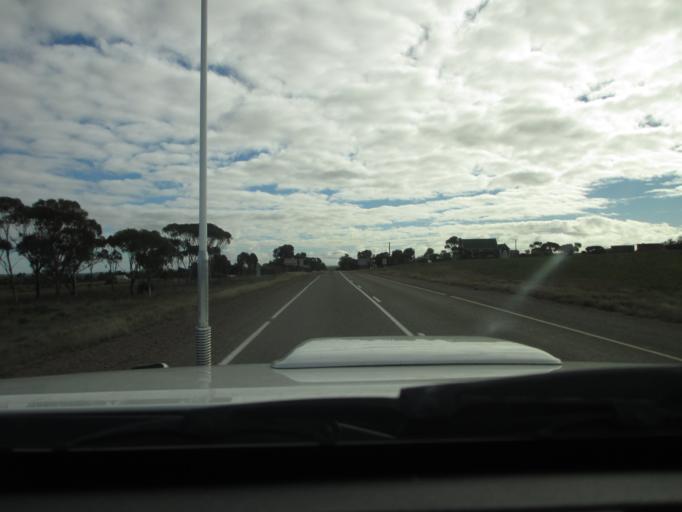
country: AU
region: South Australia
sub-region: Flinders Ranges
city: Quorn
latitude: -32.4284
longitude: 138.5312
